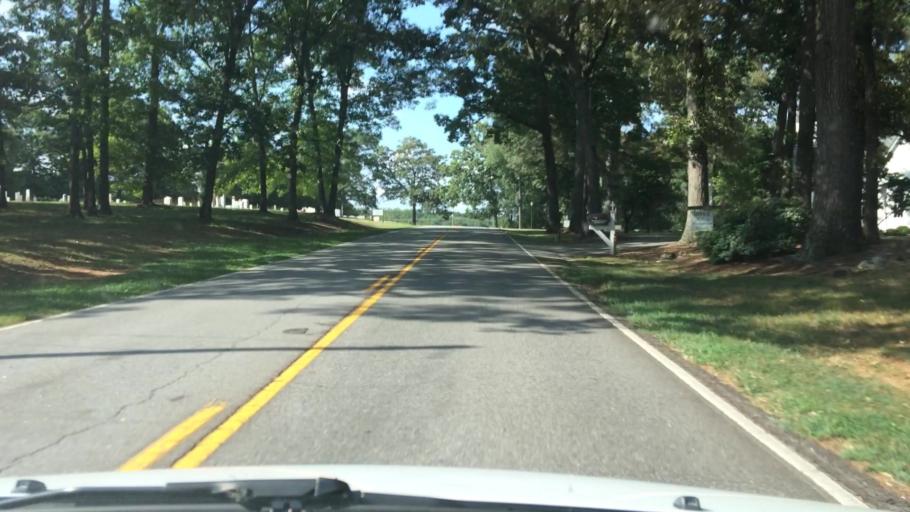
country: US
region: South Carolina
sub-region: Anderson County
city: Anderson
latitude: 34.5605
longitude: -82.6107
